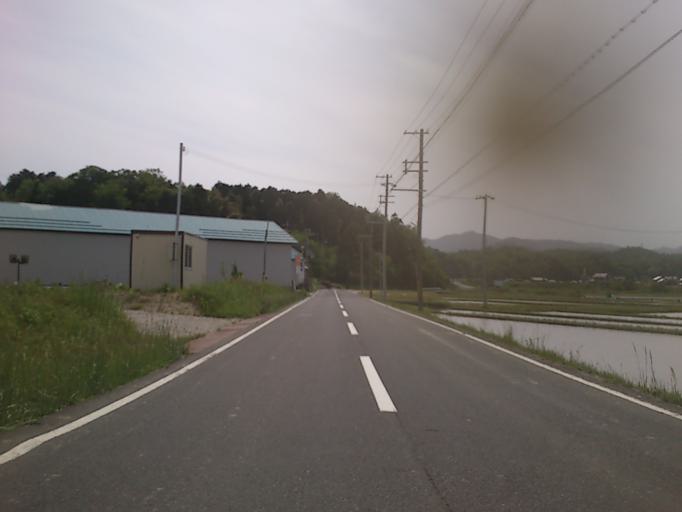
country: JP
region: Kyoto
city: Miyazu
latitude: 35.6414
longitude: 135.0850
